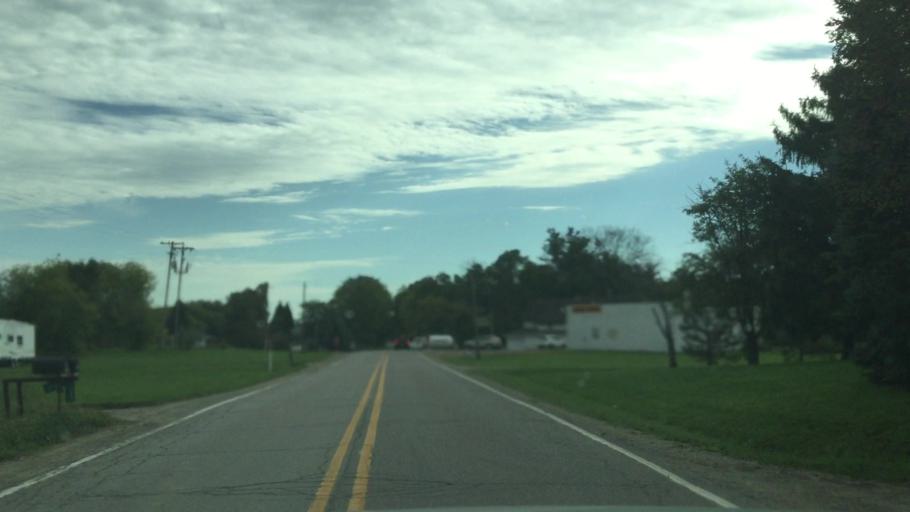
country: US
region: Michigan
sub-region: Genesee County
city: Argentine
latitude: 42.7051
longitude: -83.8425
